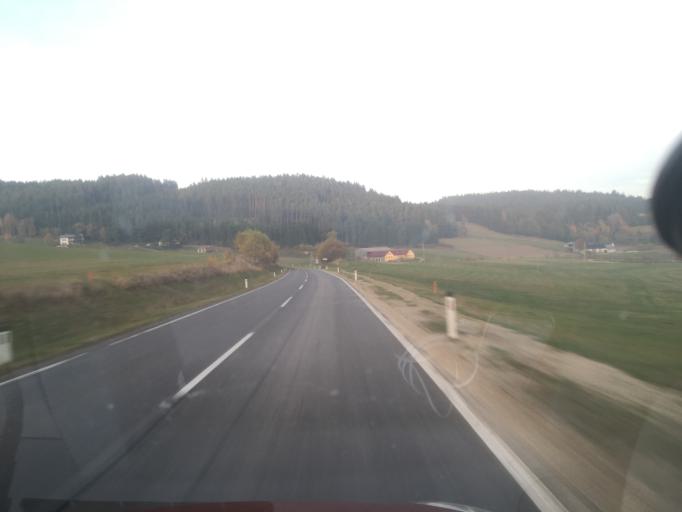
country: AT
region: Lower Austria
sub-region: Politischer Bezirk Zwettl
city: Langschlag
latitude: 48.5821
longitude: 14.8133
